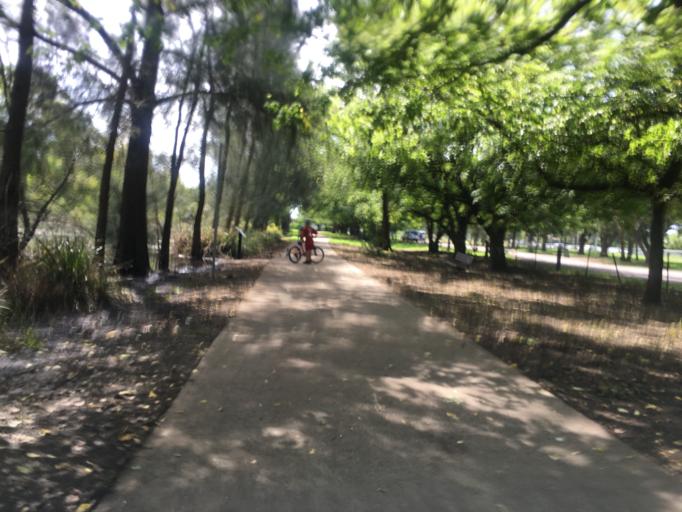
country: AU
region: New South Wales
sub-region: Camden
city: Elderslie
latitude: -34.0556
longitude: 150.7007
